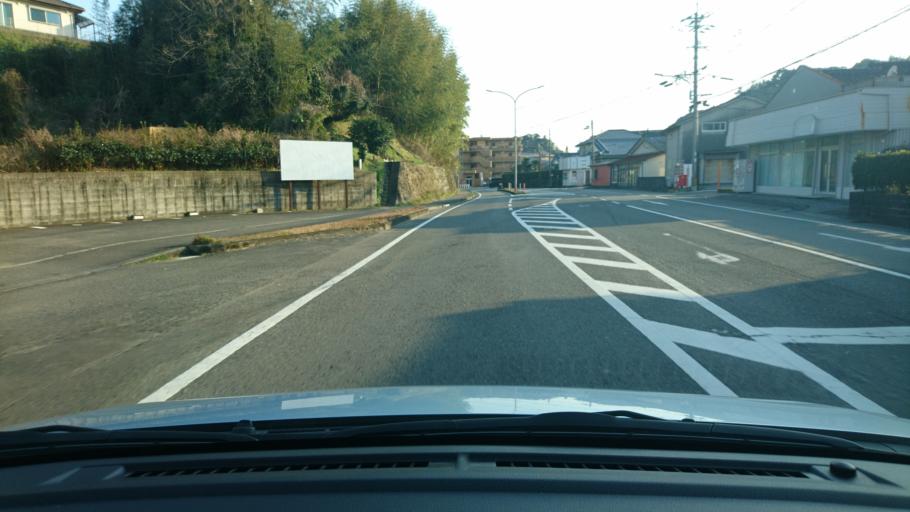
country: JP
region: Miyazaki
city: Miyazaki-shi
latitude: 31.9724
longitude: 131.4398
